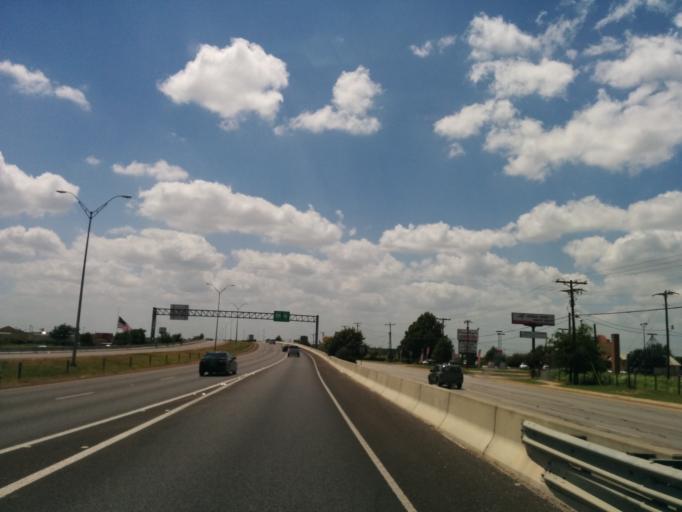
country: US
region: Texas
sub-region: Bastrop County
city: Bastrop
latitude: 30.1111
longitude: -97.3457
